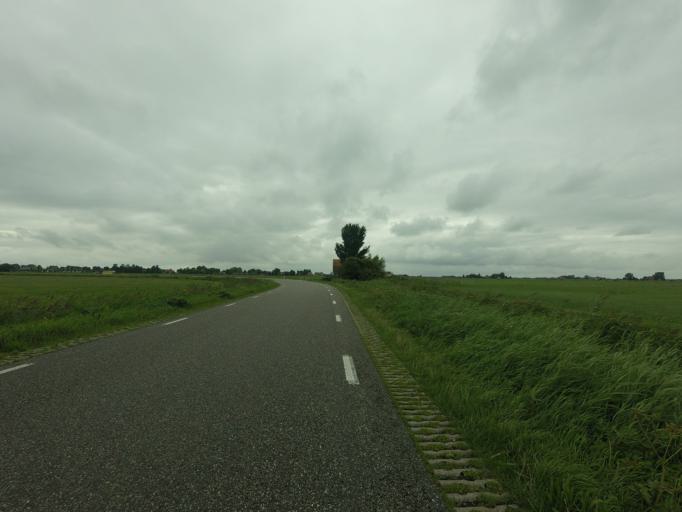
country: NL
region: Friesland
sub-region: Sudwest Fryslan
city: Heeg
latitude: 52.9696
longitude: 5.5493
